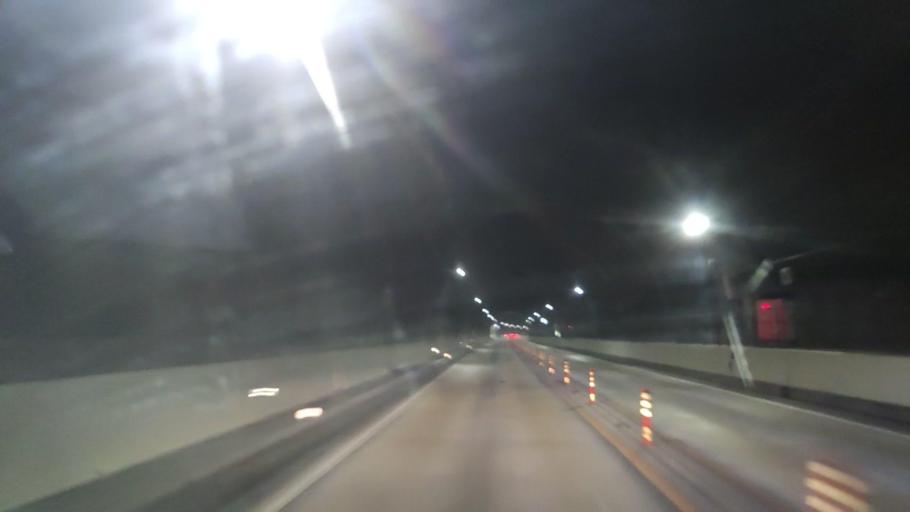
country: JP
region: Hiroshima
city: Innoshima
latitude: 34.1798
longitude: 133.0684
